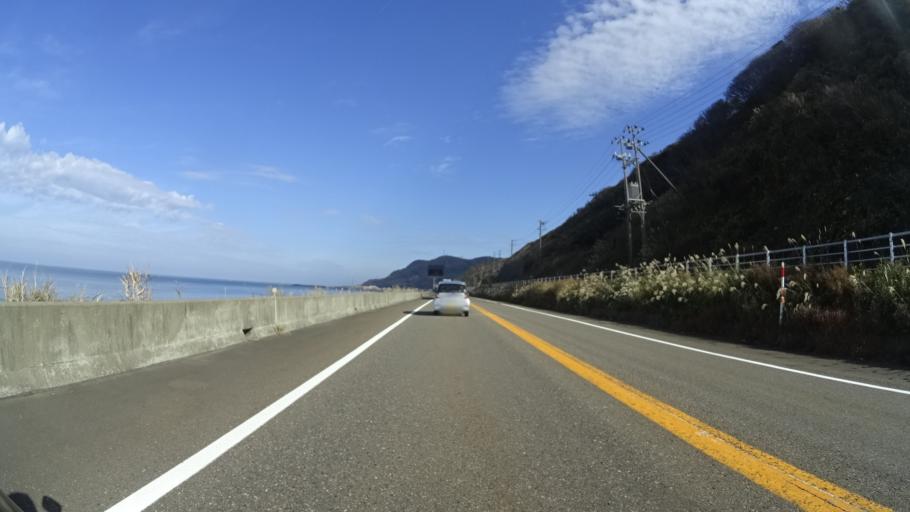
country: JP
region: Niigata
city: Joetsu
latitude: 37.1505
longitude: 138.0718
